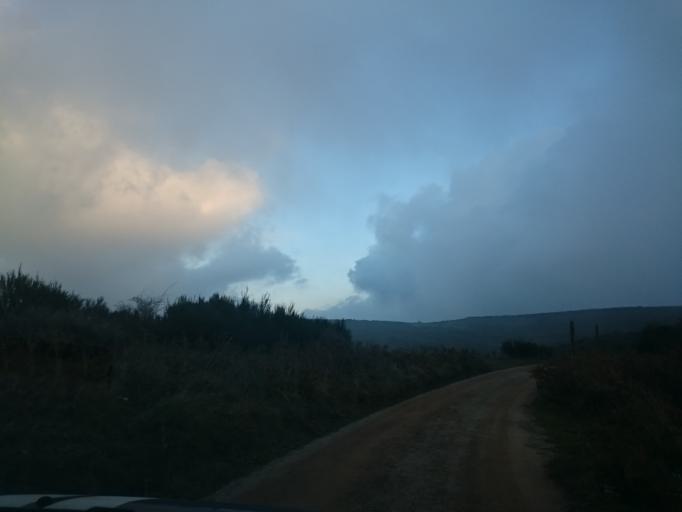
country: ES
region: Catalonia
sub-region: Provincia de Barcelona
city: Tagamanent
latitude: 41.7666
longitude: 2.3332
